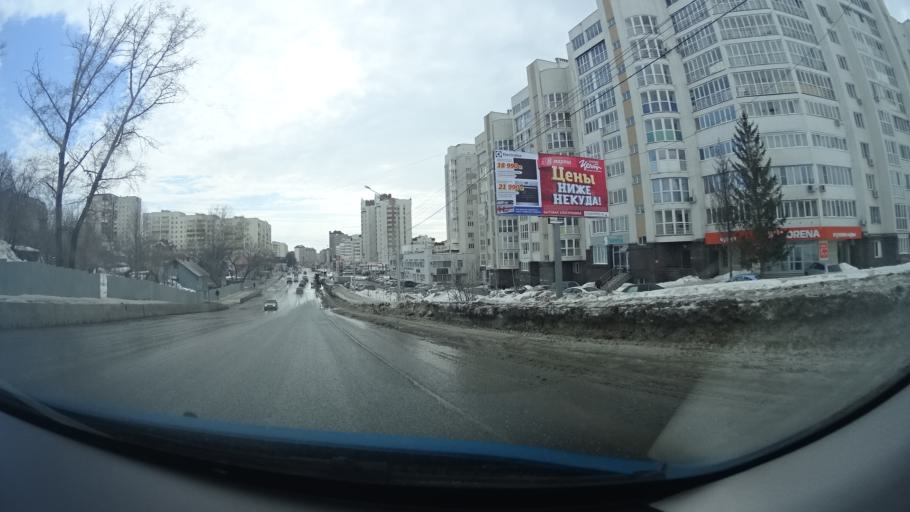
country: RU
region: Bashkortostan
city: Ufa
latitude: 54.6997
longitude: 55.9813
